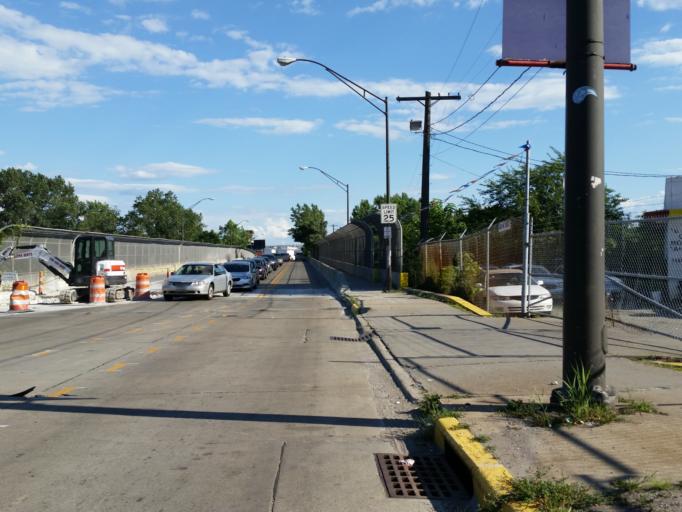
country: US
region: Ohio
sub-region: Cuyahoga County
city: Cleveland
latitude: 41.4805
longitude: -81.7007
